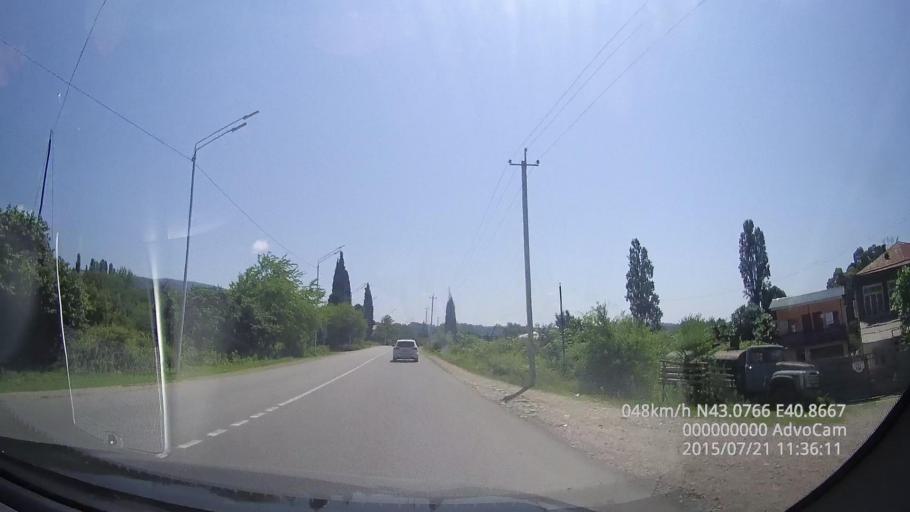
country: GE
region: Abkhazia
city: Stantsiya Novyy Afon
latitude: 43.0765
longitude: 40.8672
